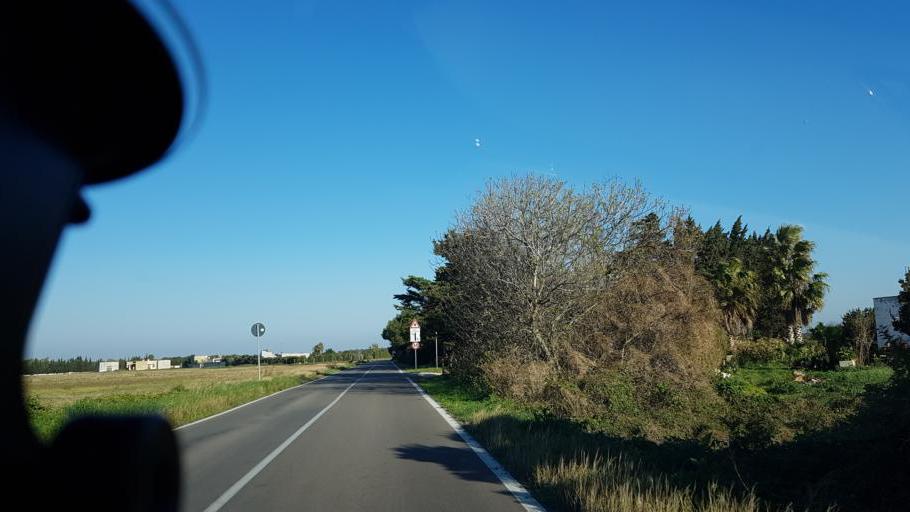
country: IT
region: Apulia
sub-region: Provincia di Lecce
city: Struda
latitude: 40.3931
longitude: 18.2776
